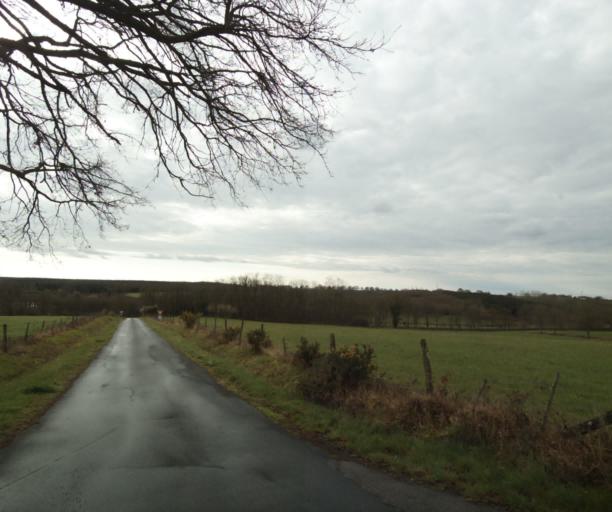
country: FR
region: Auvergne
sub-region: Departement de l'Allier
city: Toulon-sur-Allier
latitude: 46.5175
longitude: 3.3776
